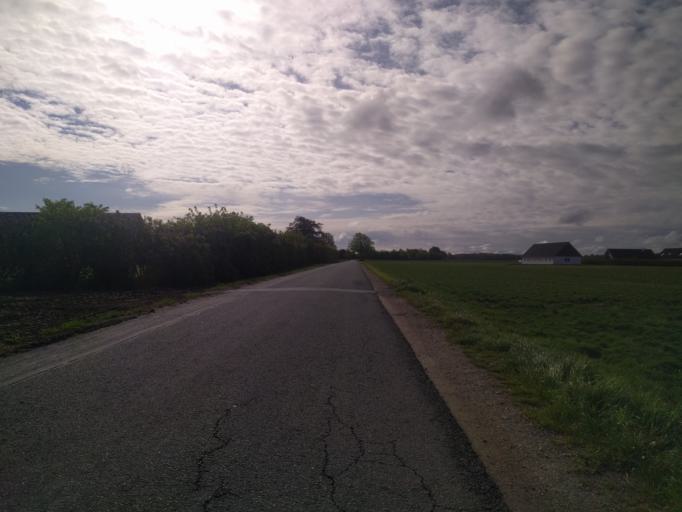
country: DK
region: South Denmark
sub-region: Kerteminde Kommune
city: Kerteminde
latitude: 55.4252
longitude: 10.6383
